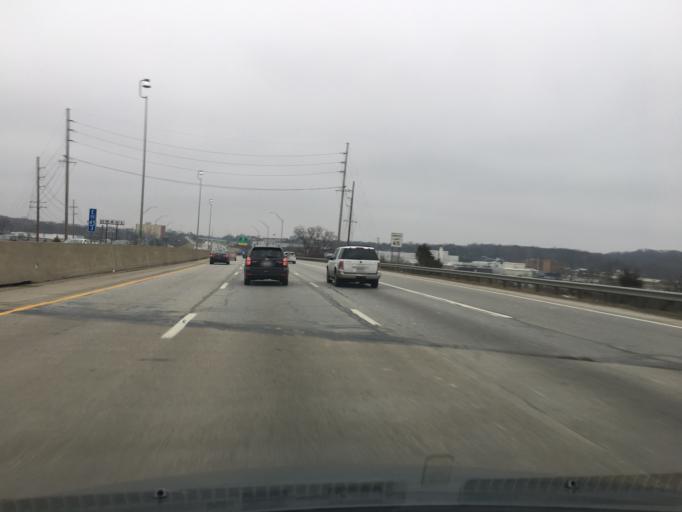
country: US
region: Ohio
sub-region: Hamilton County
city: Sharonville
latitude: 39.2849
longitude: -84.4131
